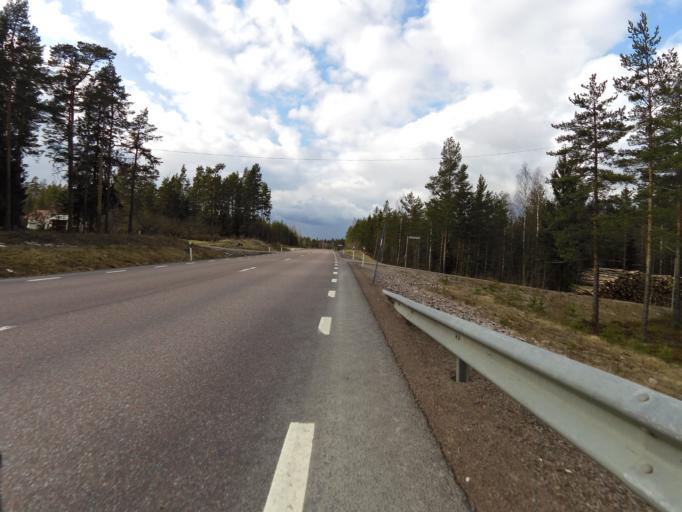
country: SE
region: Gaevleborg
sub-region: Hofors Kommun
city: Hofors
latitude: 60.4921
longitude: 16.4398
